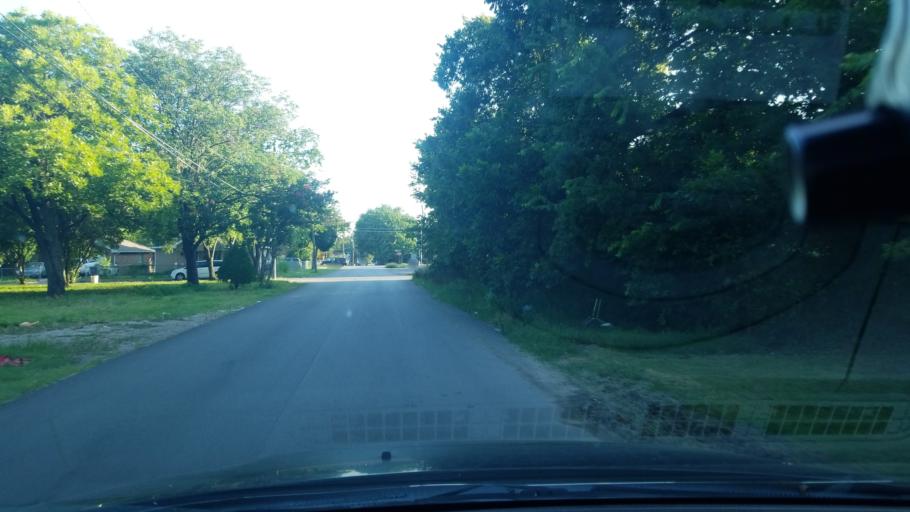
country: US
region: Texas
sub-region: Dallas County
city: Cockrell Hill
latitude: 32.7189
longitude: -96.8247
